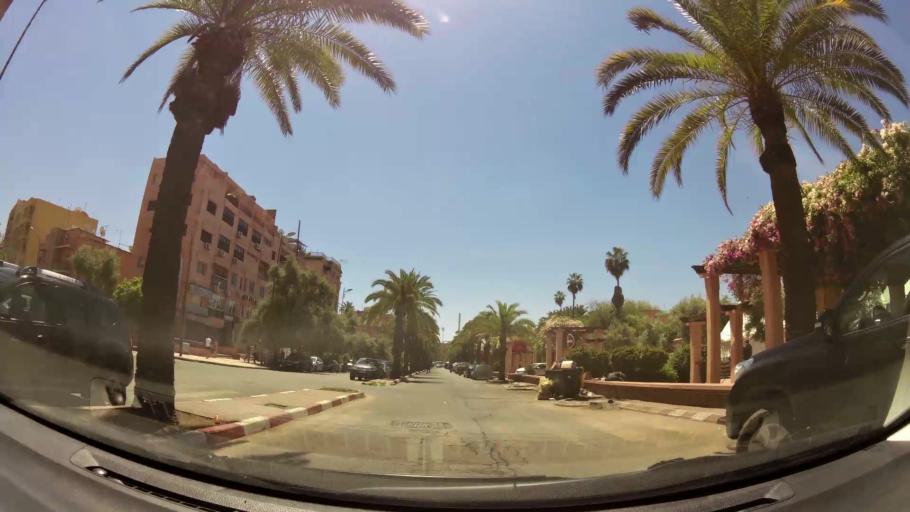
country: MA
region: Marrakech-Tensift-Al Haouz
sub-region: Marrakech
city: Marrakesh
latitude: 31.6313
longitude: -8.0084
